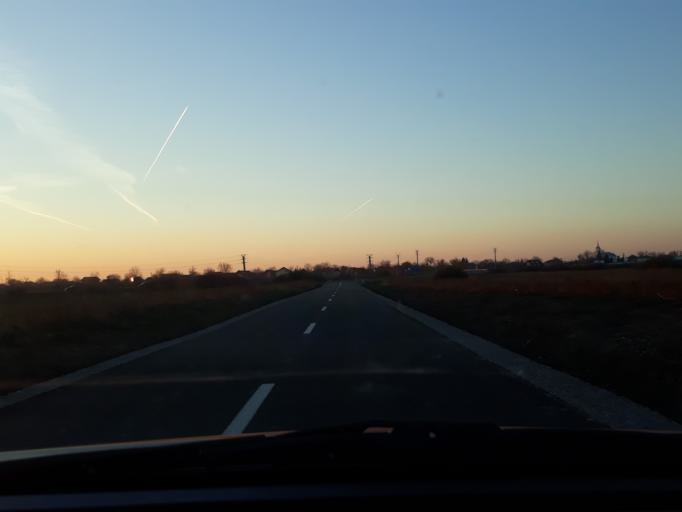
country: RO
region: Bihor
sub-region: Comuna Gepiu
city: Gepiu
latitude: 46.9201
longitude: 21.7839
